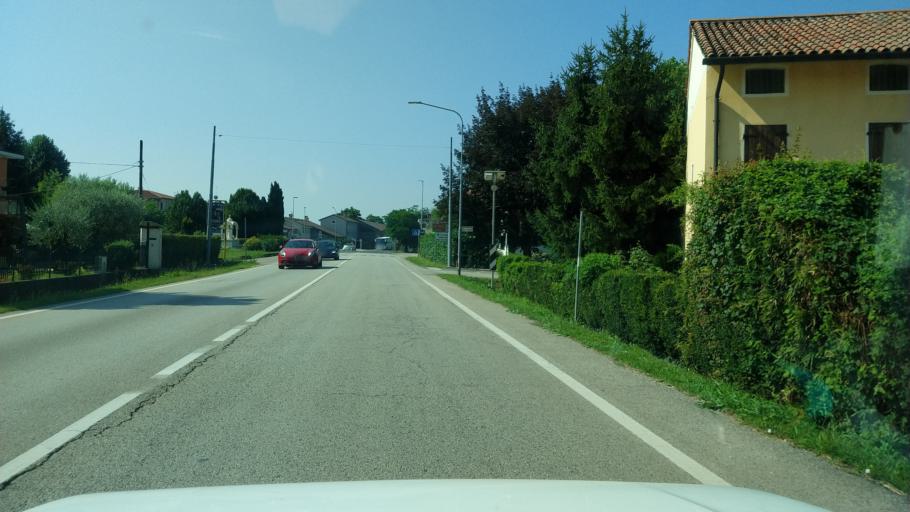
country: IT
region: Veneto
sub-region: Provincia di Vicenza
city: Bressanvido
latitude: 45.6654
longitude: 11.6353
